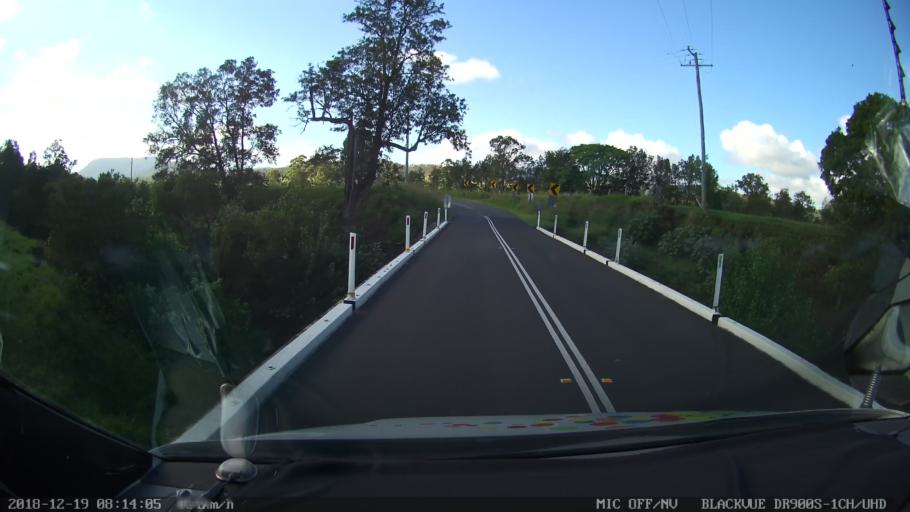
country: AU
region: Queensland
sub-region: Logan
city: Cedar Vale
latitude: -28.2450
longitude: 152.8900
